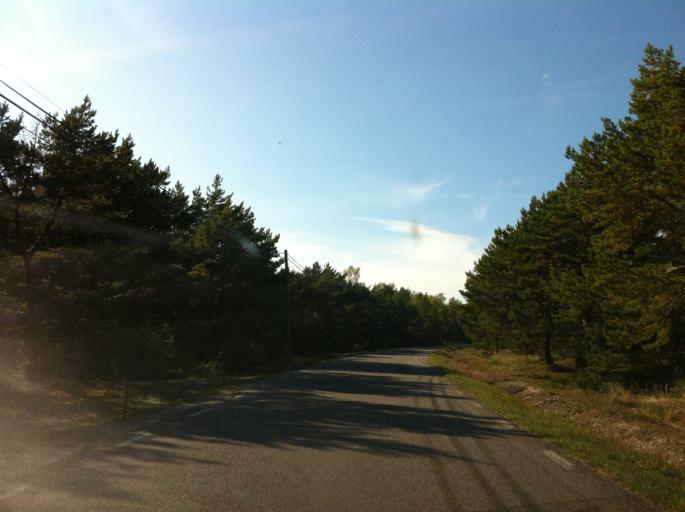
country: SE
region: Gotland
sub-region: Gotland
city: Slite
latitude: 57.9714
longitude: 19.2553
